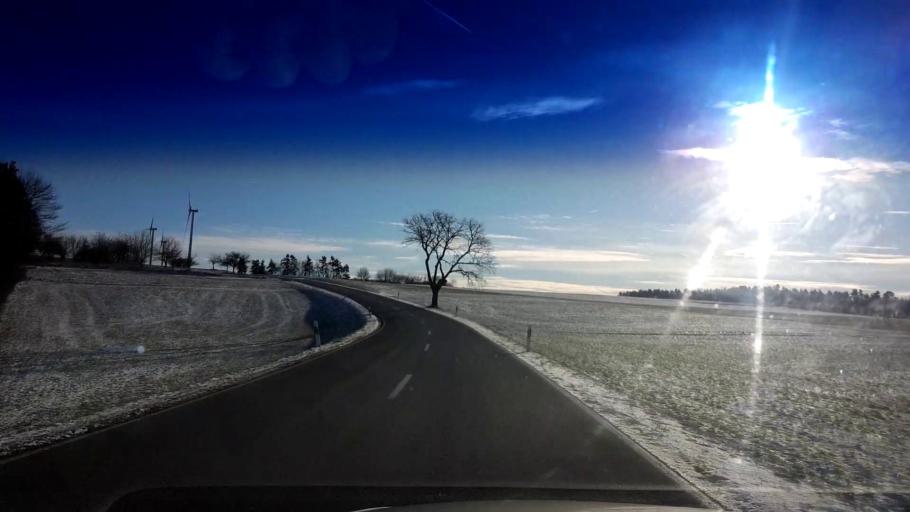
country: DE
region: Bavaria
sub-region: Upper Franconia
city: Poxdorf
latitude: 49.8664
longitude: 11.0889
